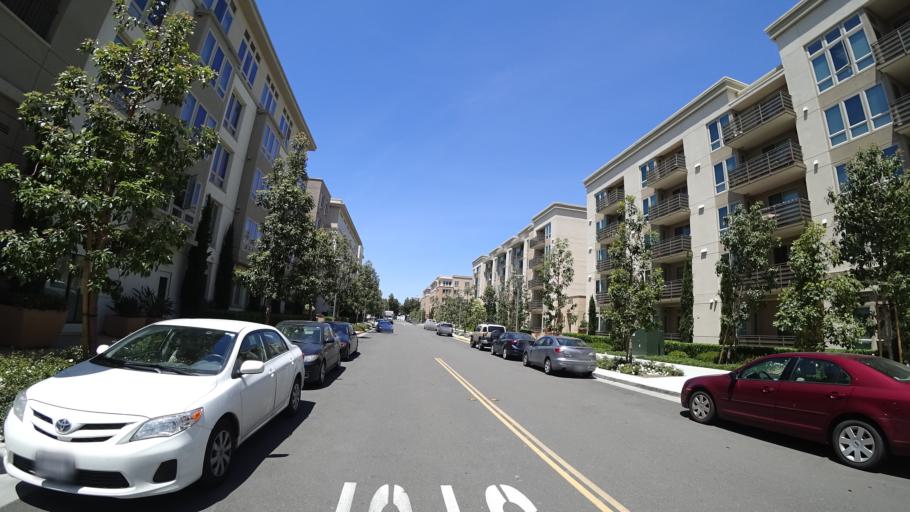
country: US
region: California
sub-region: Santa Clara County
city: Milpitas
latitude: 37.4023
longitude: -121.9421
